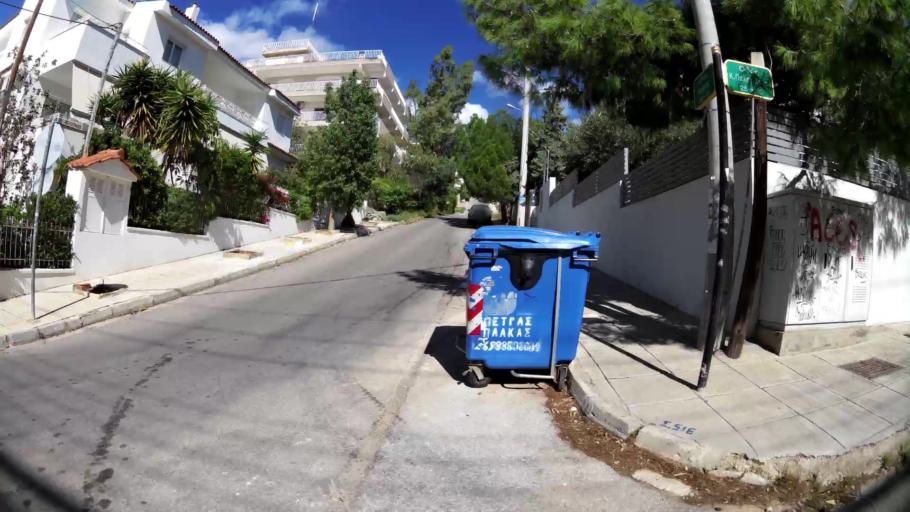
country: GR
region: Attica
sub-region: Nomarchia Anatolikis Attikis
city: Voula
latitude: 37.8468
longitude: 23.7747
